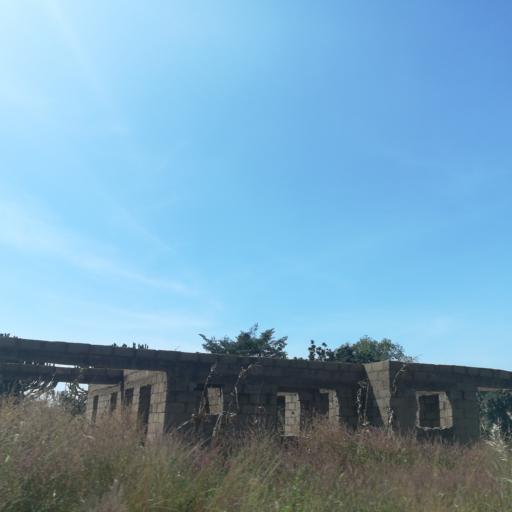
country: NG
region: Plateau
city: Bukuru
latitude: 9.7582
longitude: 8.8680
